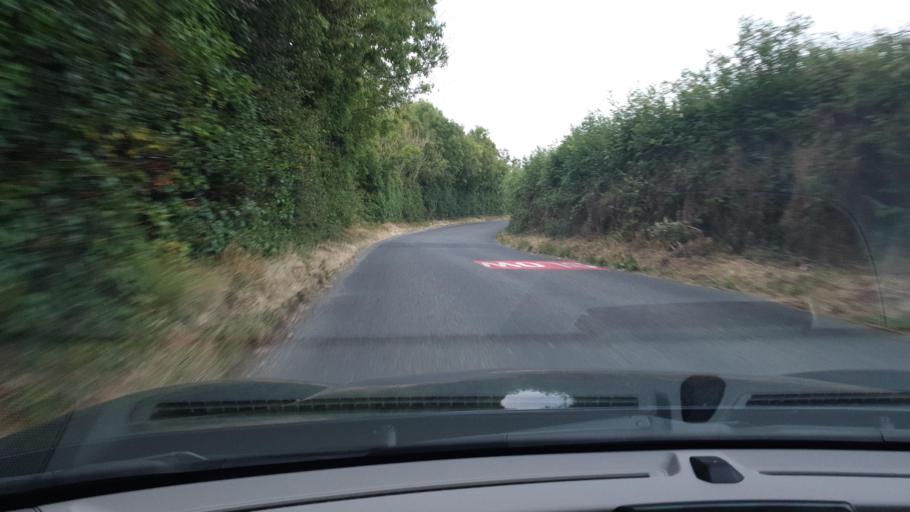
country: IE
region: Leinster
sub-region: An Mhi
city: Ashbourne
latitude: 53.5023
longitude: -6.3813
